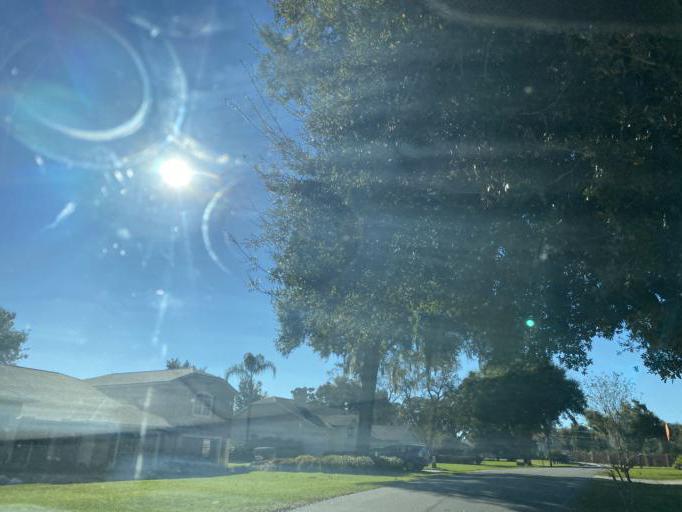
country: US
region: Florida
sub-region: Lake County
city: Howie In The Hills
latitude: 28.7316
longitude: -81.7682
